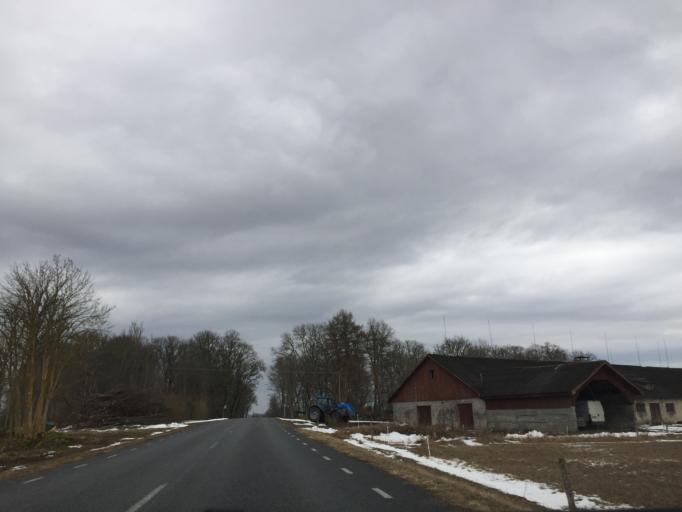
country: EE
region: Saare
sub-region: Orissaare vald
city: Orissaare
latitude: 58.5543
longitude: 22.7746
